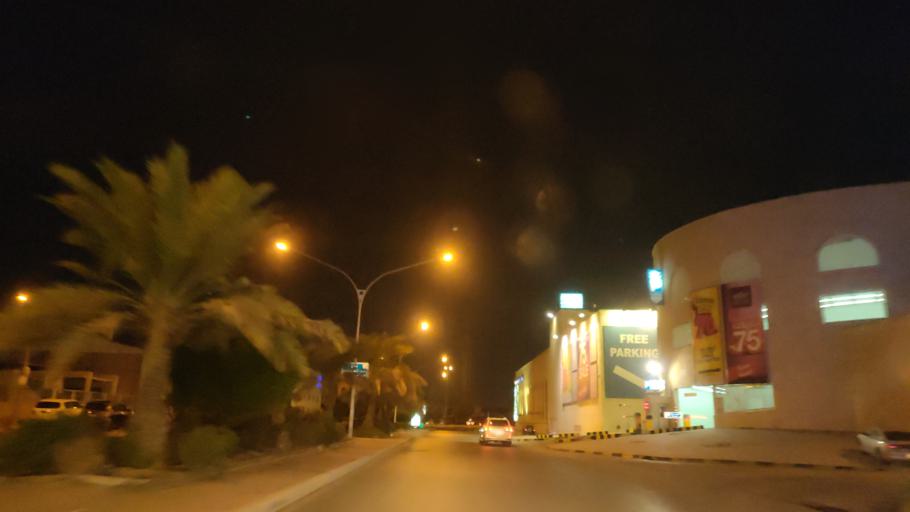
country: KW
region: Al Asimah
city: Ar Rabiyah
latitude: 29.3121
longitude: 47.9345
